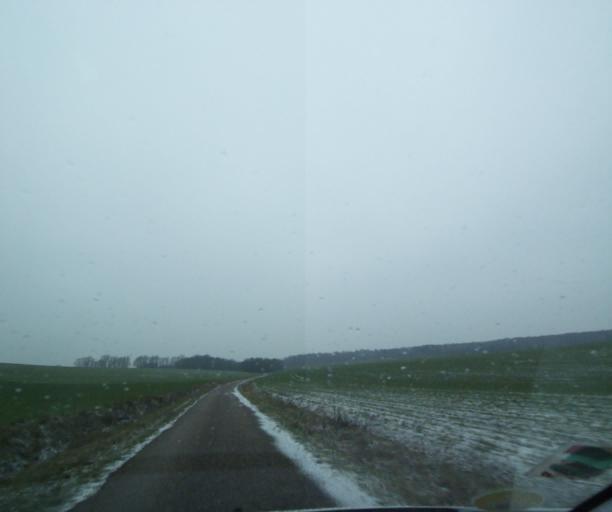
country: FR
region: Champagne-Ardenne
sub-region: Departement de la Haute-Marne
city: Wassy
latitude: 48.4626
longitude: 5.0245
